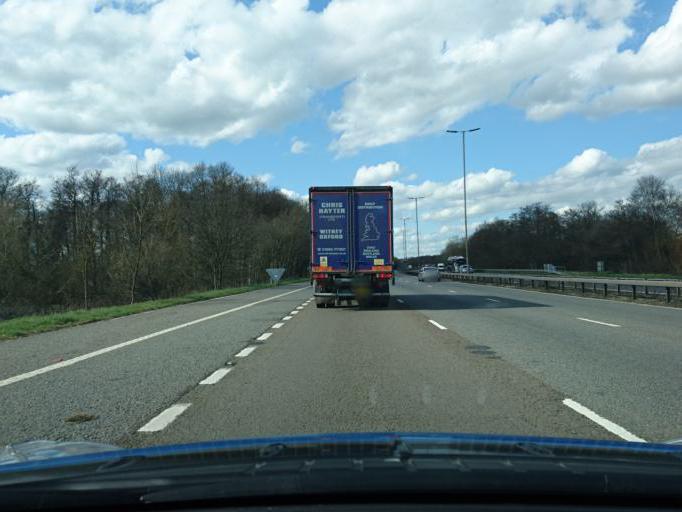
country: GB
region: England
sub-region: West Berkshire
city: Theale
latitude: 51.4432
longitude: -1.0714
